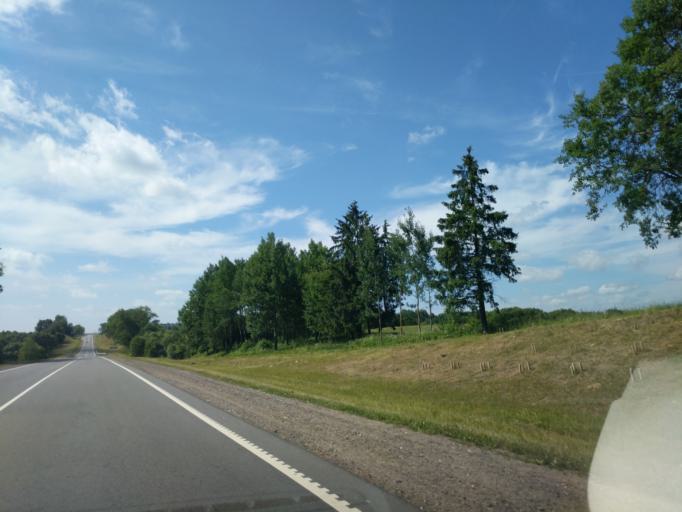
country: BY
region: Minsk
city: Syomkava
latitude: 54.1040
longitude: 27.4731
